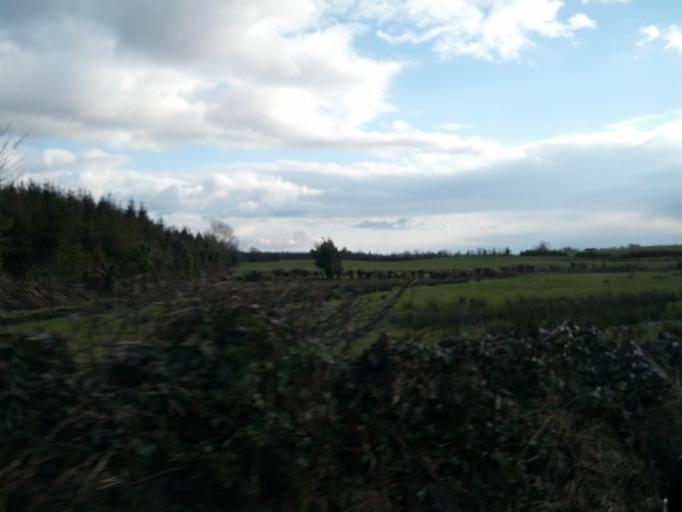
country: IE
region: Connaught
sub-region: County Galway
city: Athenry
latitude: 53.3759
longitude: -8.6302
